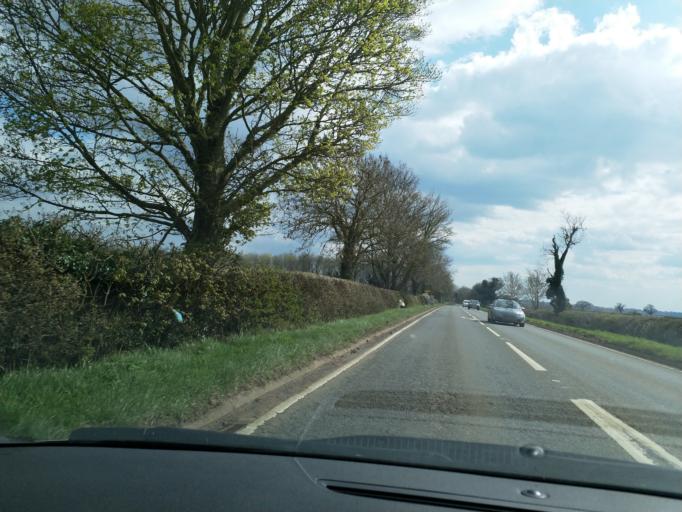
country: GB
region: England
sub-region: Oxfordshire
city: Hanwell
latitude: 52.0904
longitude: -1.3739
